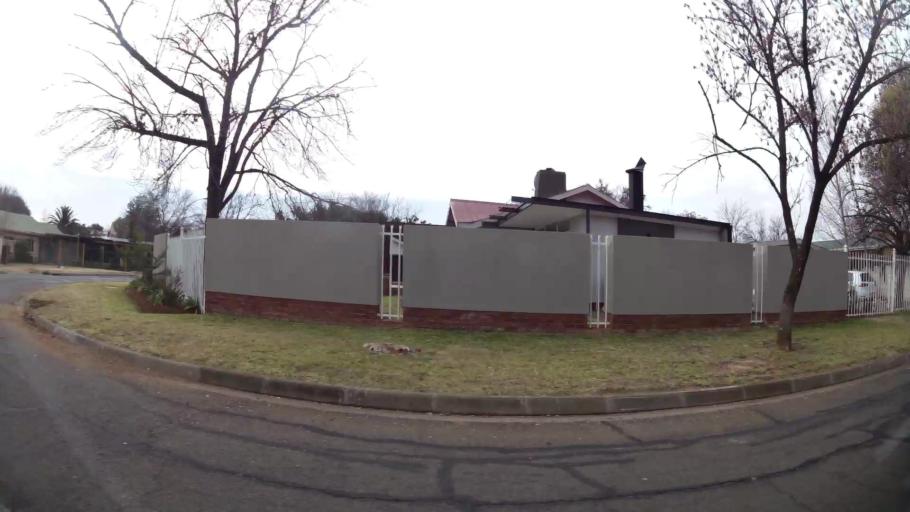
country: ZA
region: Orange Free State
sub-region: Mangaung Metropolitan Municipality
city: Bloemfontein
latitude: -29.1239
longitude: 26.1693
